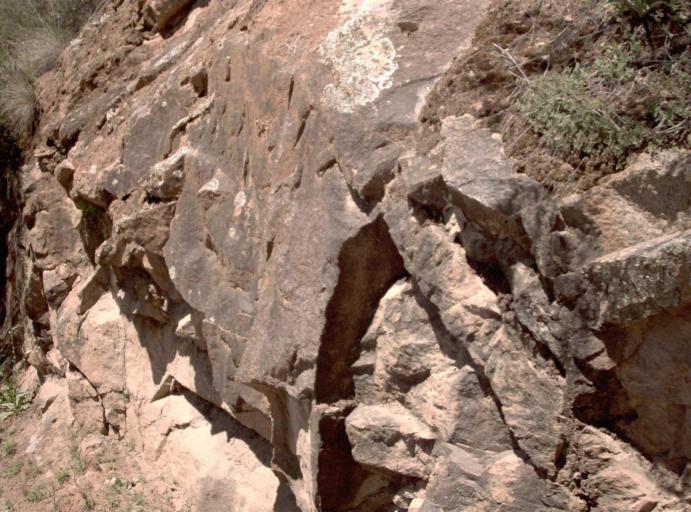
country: AU
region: New South Wales
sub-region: Snowy River
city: Jindabyne
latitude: -37.0362
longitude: 148.5410
